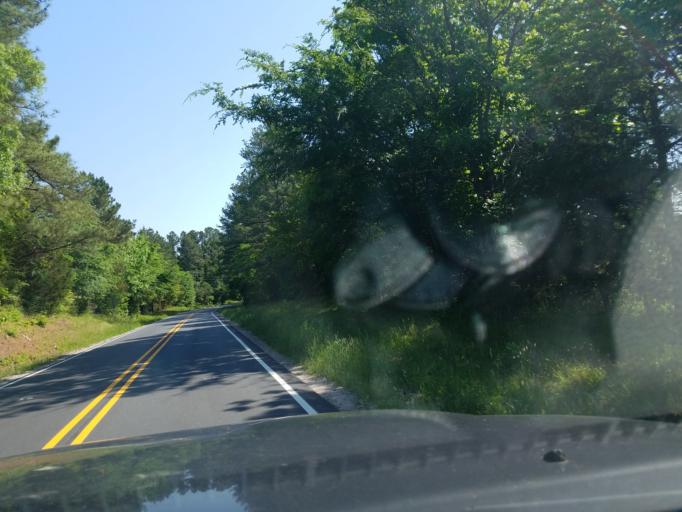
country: US
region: North Carolina
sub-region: Vance County
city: Henderson
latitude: 36.3673
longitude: -78.4528
